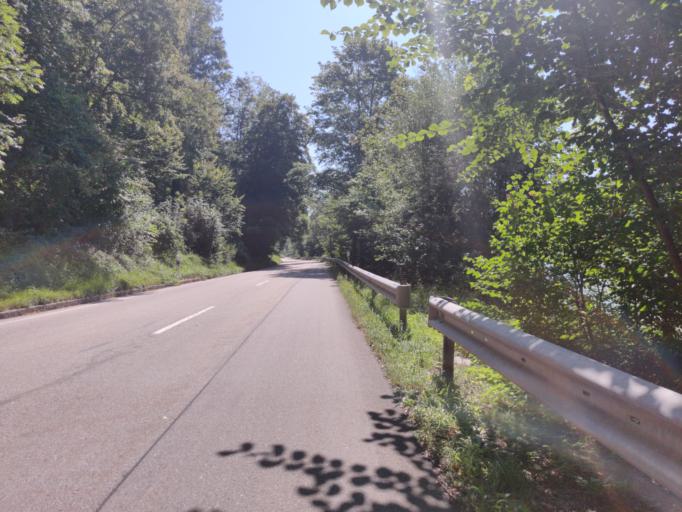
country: DE
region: Bavaria
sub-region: Lower Bavaria
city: Untergriesbach
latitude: 48.5298
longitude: 13.6849
